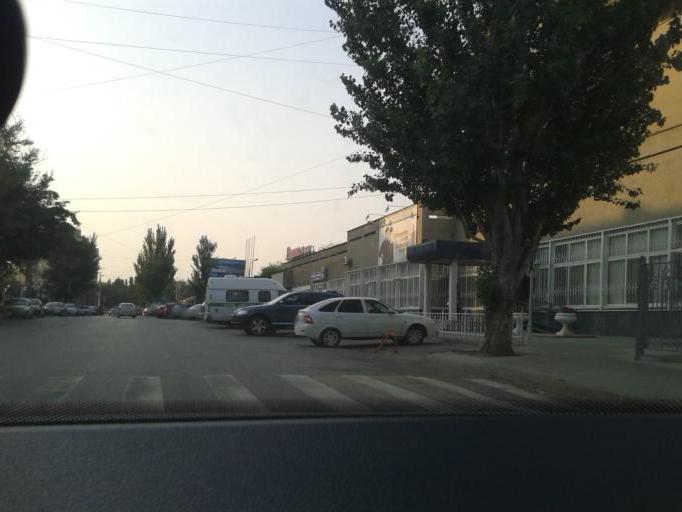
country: RU
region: Volgograd
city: Volgograd
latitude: 48.6992
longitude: 44.5076
